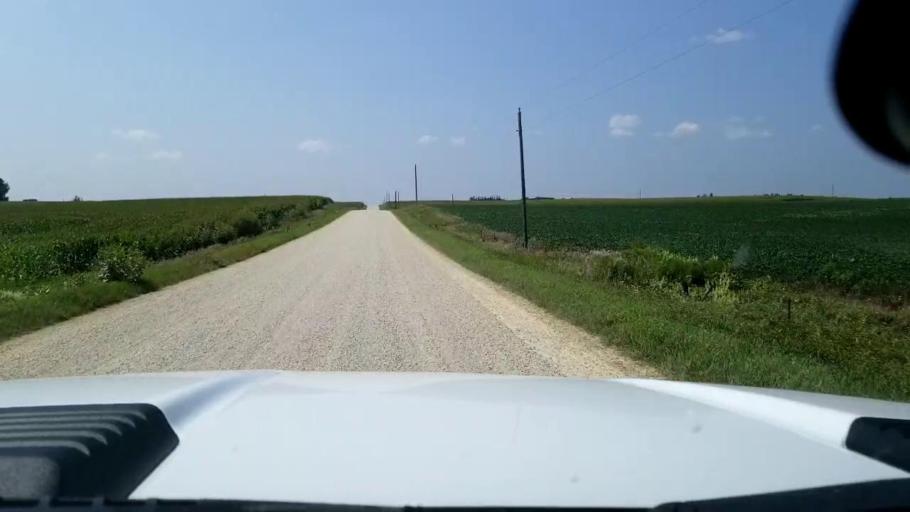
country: US
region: Minnesota
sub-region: Goodhue County
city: Wanamingo
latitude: 44.3416
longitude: -92.8874
